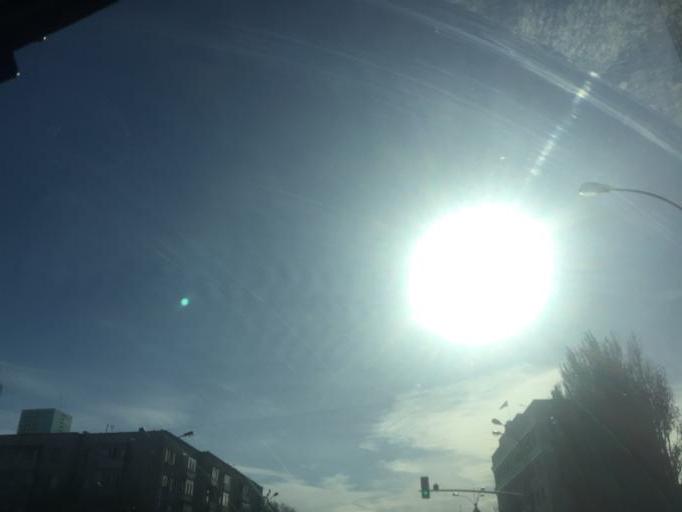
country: KZ
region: Astana Qalasy
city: Astana
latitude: 51.1657
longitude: 71.4138
